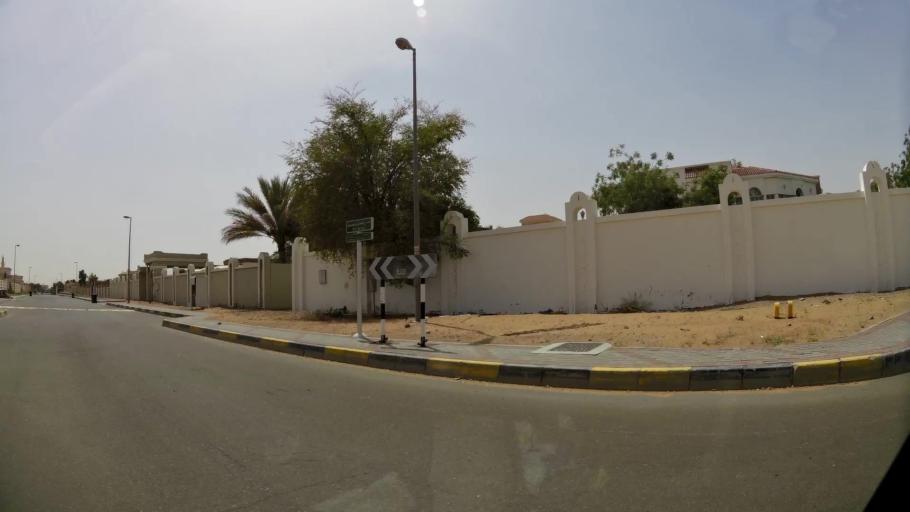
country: AE
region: Abu Dhabi
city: Al Ain
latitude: 24.1503
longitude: 55.6467
